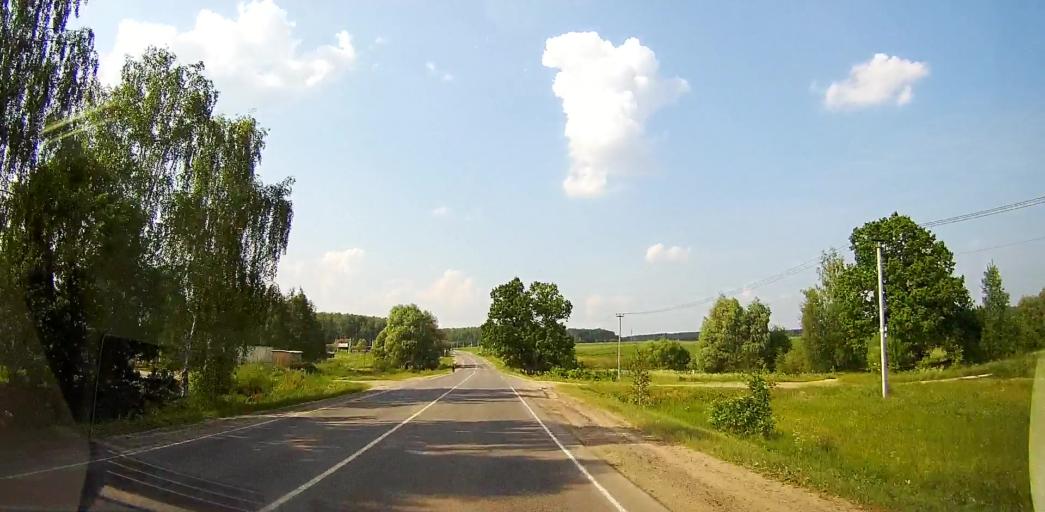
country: RU
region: Moskovskaya
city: Il'inskoye
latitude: 55.2042
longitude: 37.9625
